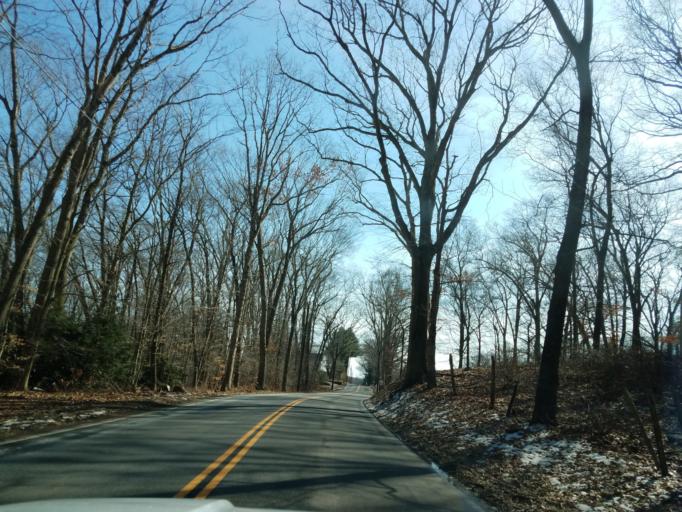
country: US
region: Rhode Island
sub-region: Washington County
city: Hopkinton
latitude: 41.4522
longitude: -71.8114
